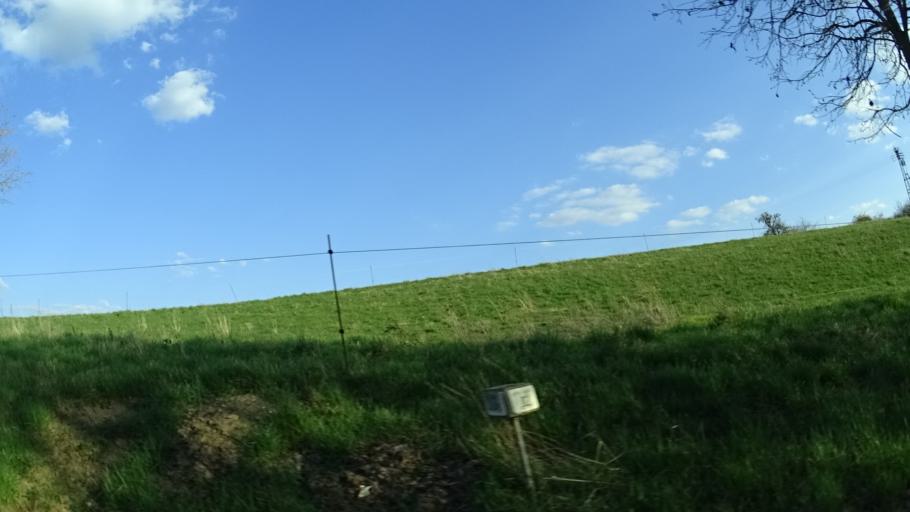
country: DE
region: Rheinland-Pfalz
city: Lettweiler
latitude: 49.7332
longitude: 7.7275
